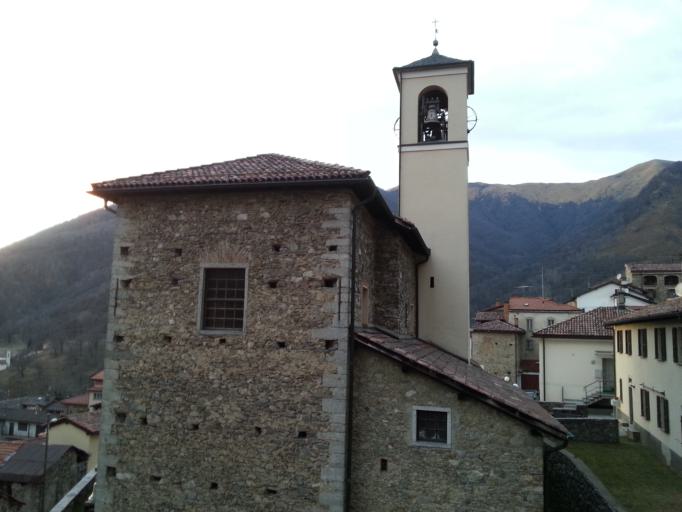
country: CH
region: Ticino
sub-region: Lugano District
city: Gravesano
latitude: 46.0486
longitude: 8.8906
